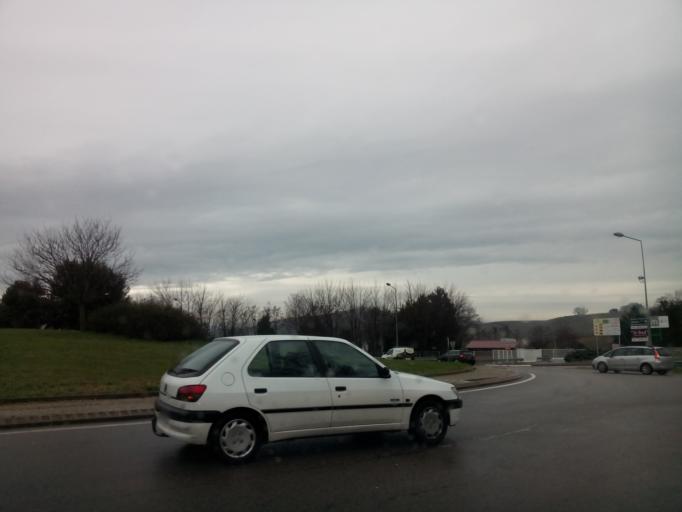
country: FR
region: Rhone-Alpes
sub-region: Departement de la Drome
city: Mercurol
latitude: 45.0703
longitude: 4.8648
